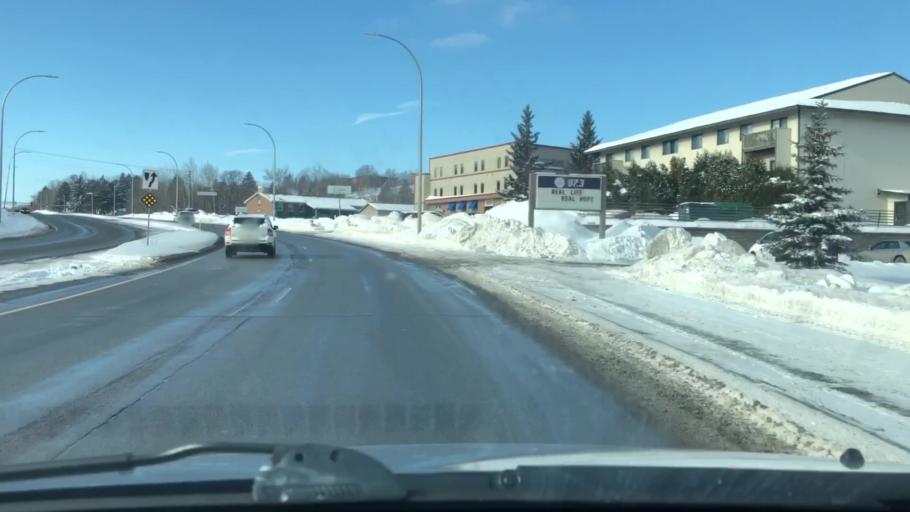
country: US
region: Minnesota
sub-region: Saint Louis County
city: Duluth
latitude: 46.7991
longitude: -92.1113
